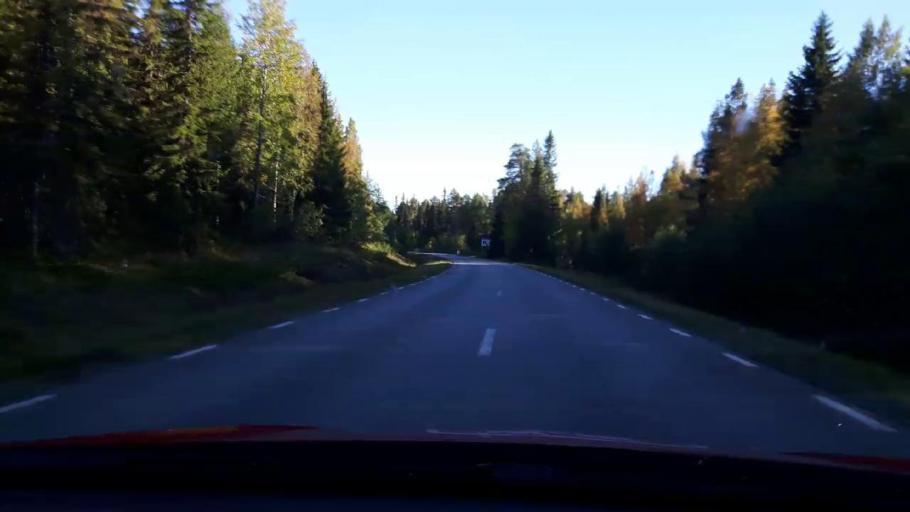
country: SE
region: Jaemtland
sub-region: OEstersunds Kommun
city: Lit
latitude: 63.7526
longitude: 14.7154
